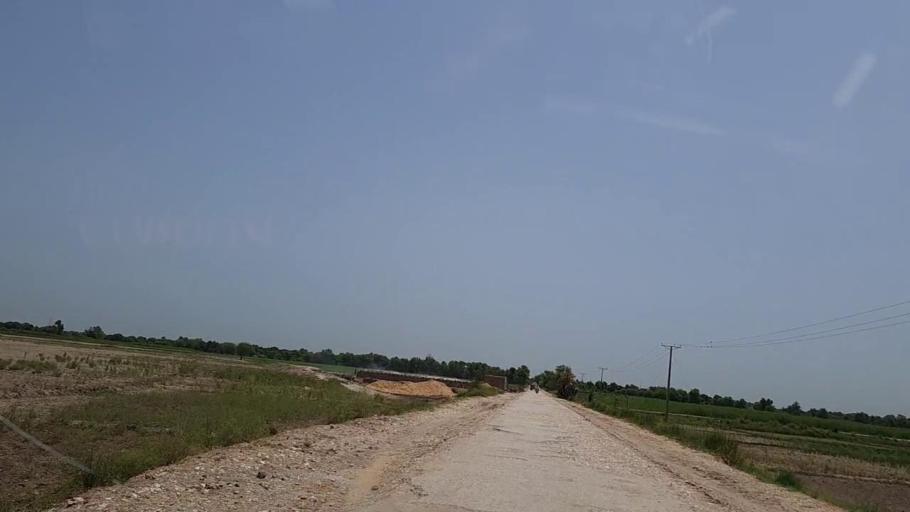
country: PK
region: Sindh
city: Tharu Shah
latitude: 26.9510
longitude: 68.0924
